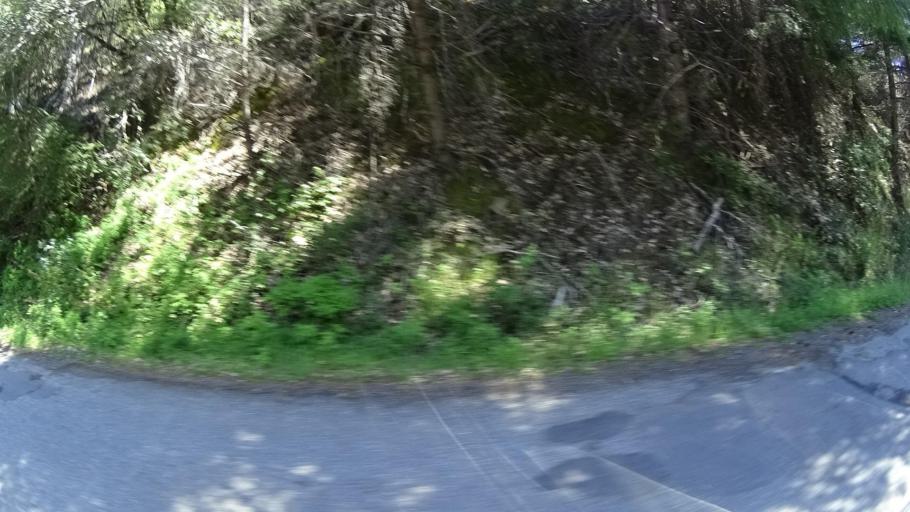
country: US
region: California
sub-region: Humboldt County
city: Rio Dell
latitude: 40.2621
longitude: -124.1137
